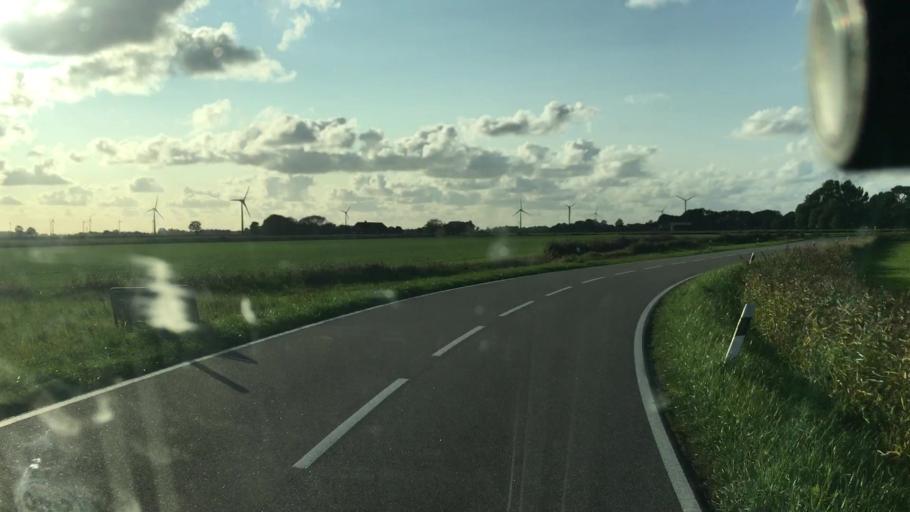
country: DE
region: Lower Saxony
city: Wittmund
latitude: 53.6342
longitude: 7.8313
